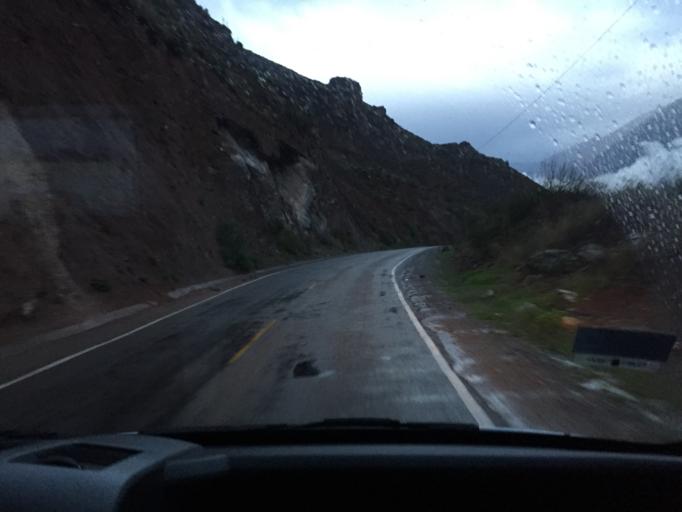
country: PE
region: Cusco
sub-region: Provincia de Urubamba
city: Urubamba
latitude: -13.3128
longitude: -72.1184
